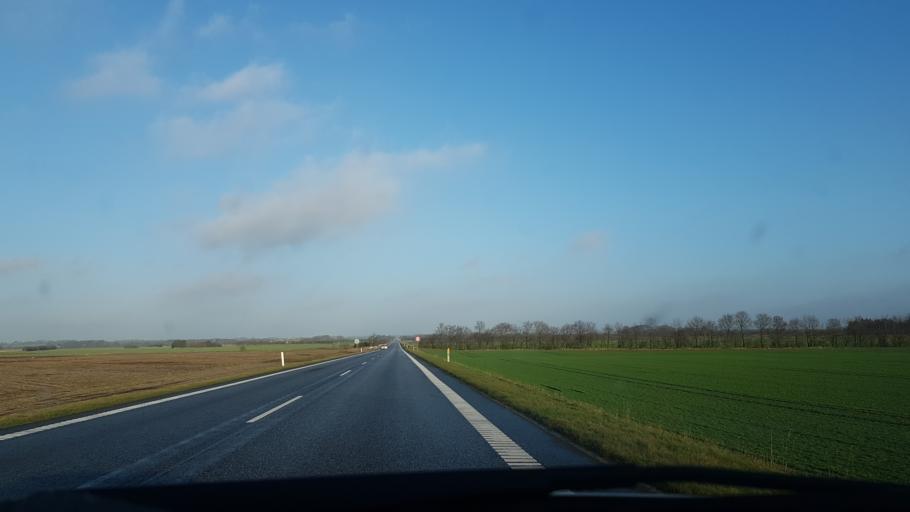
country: DK
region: South Denmark
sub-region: Tonder Kommune
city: Toftlund
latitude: 55.2154
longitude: 9.1016
